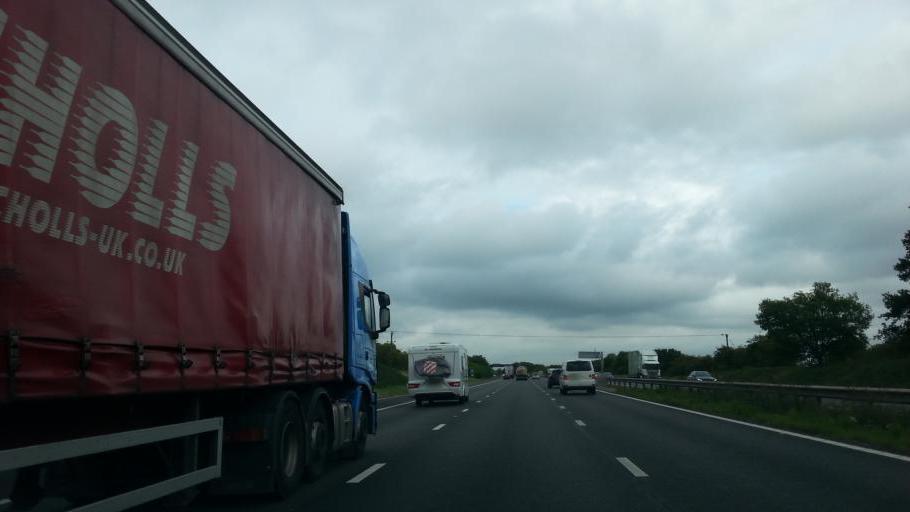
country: GB
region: England
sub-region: Leicestershire
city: Enderby
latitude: 52.5888
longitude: -1.1968
